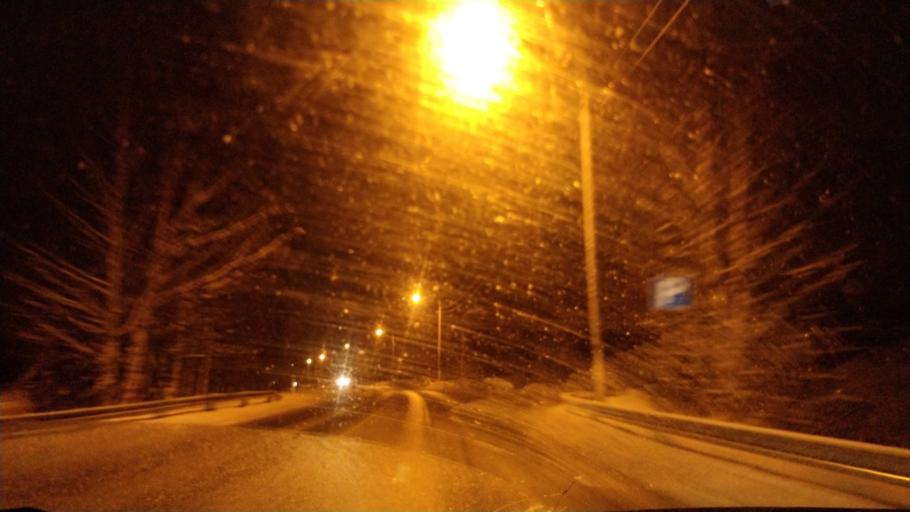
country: FI
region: Lapland
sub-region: Rovaniemi
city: Rovaniemi
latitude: 66.3927
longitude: 25.3804
